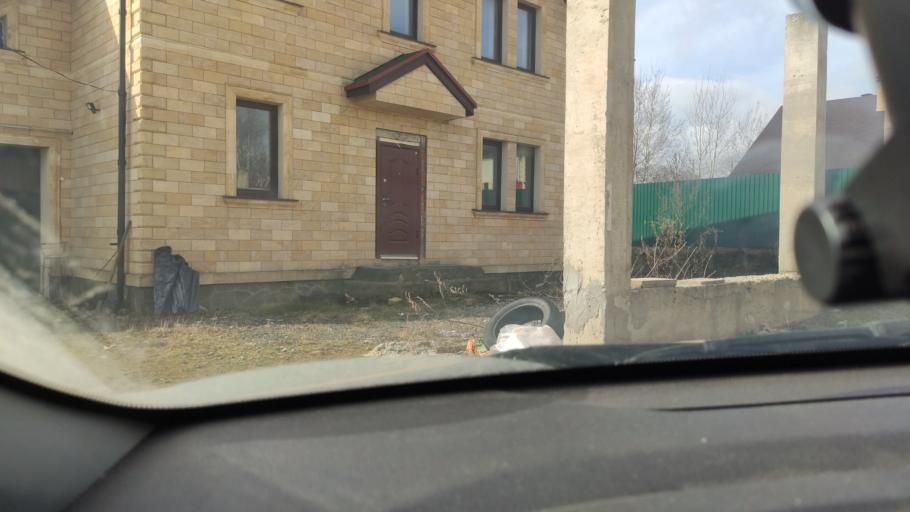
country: RU
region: Moskovskaya
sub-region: Podol'skiy Rayon
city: Podol'sk
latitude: 55.3920
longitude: 37.6287
